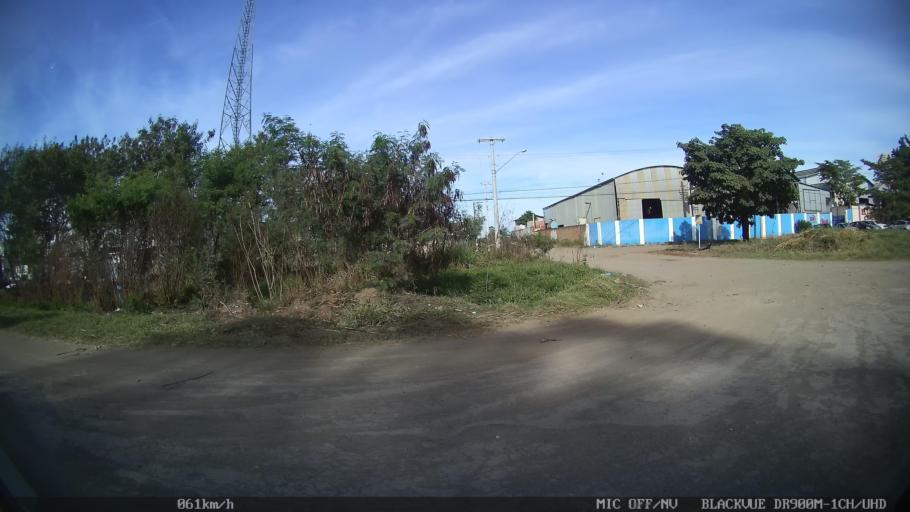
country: BR
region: Sao Paulo
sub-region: Rio Das Pedras
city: Rio das Pedras
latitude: -22.7953
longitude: -47.6148
